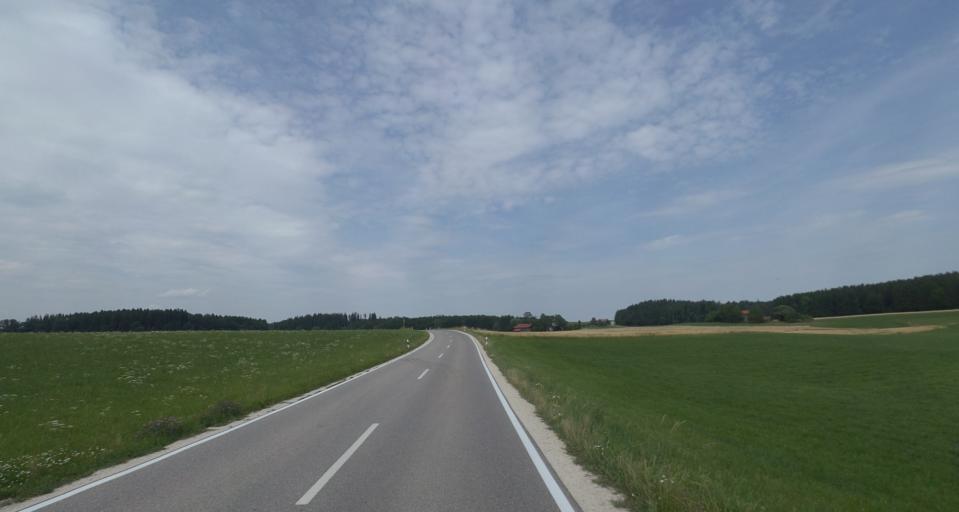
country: DE
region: Bavaria
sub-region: Upper Bavaria
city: Traunreut
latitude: 47.9469
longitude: 12.5463
